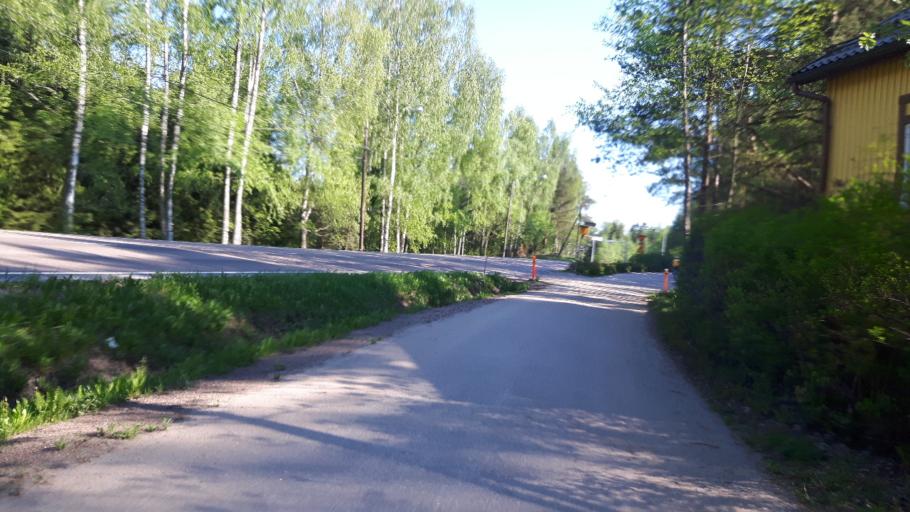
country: FI
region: Kymenlaakso
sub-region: Kotka-Hamina
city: Kotka
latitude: 60.4518
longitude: 26.8946
